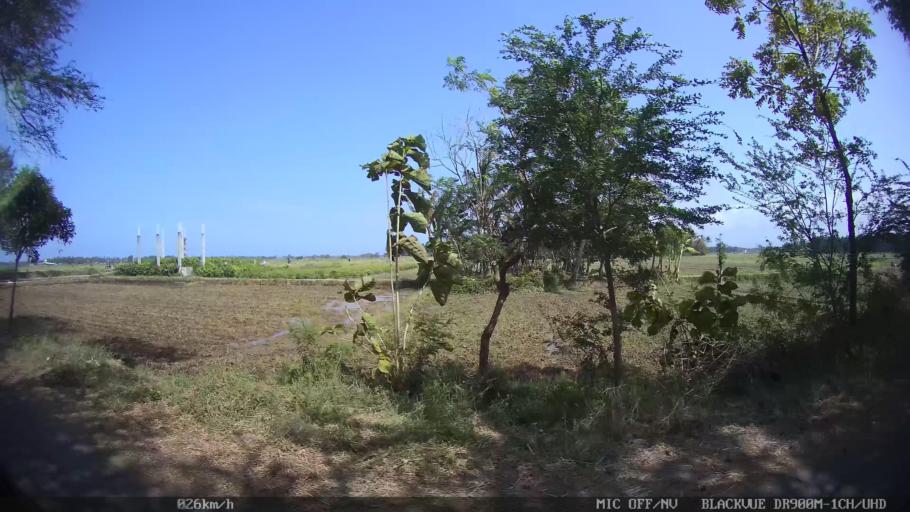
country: ID
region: Daerah Istimewa Yogyakarta
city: Srandakan
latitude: -7.9645
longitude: 110.2136
